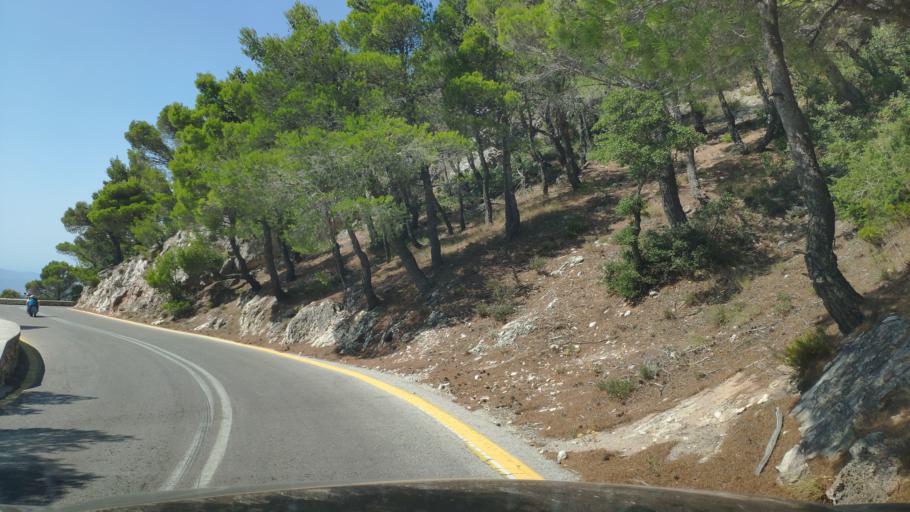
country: GR
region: Attica
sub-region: Nomarchia Anatolikis Attikis
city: Thrakomakedones
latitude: 38.1427
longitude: 23.7227
